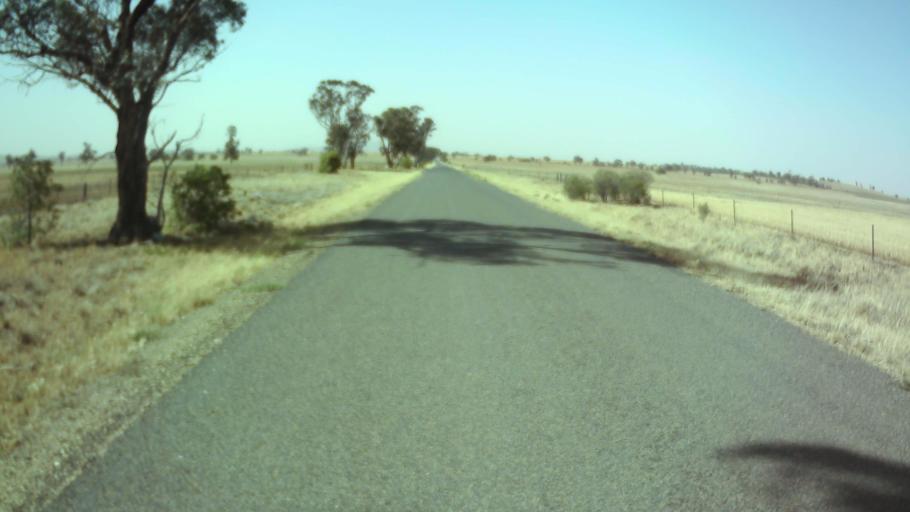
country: AU
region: New South Wales
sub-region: Weddin
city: Grenfell
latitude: -33.8747
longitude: 147.9256
